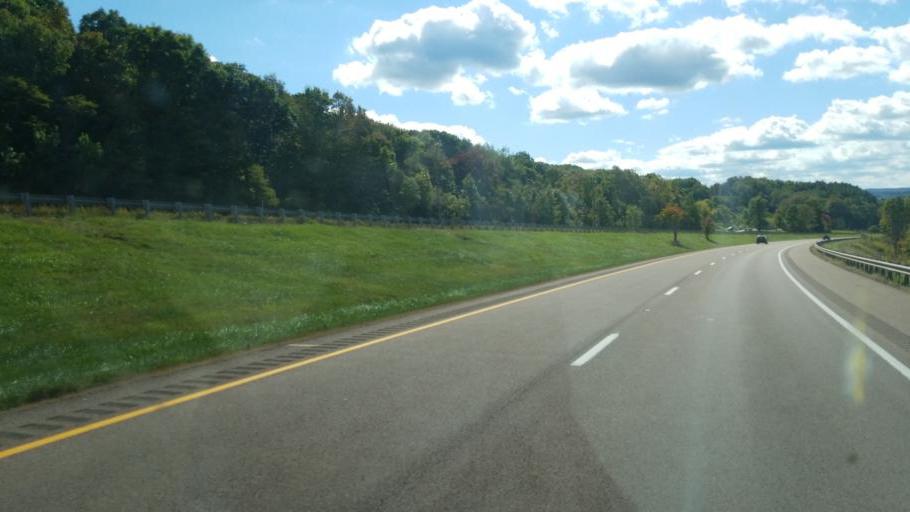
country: US
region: Maryland
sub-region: Garrett County
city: Oakland
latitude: 39.6803
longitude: -79.3698
